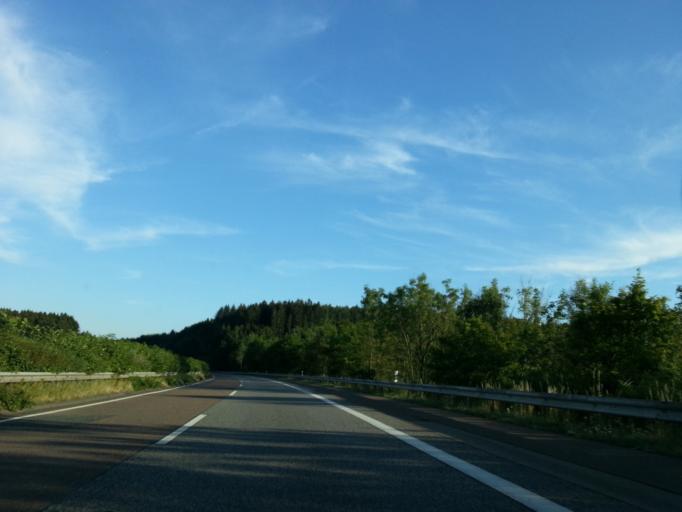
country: DE
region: Rheinland-Pfalz
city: Gusenburg
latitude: 49.6325
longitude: 6.9220
